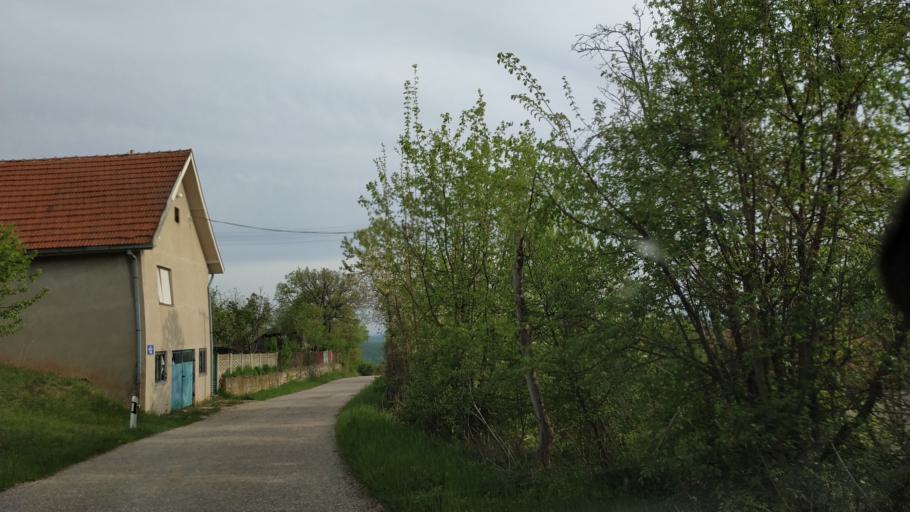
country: RS
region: Central Serbia
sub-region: Zajecarski Okrug
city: Soko Banja
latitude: 43.5390
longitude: 21.8795
